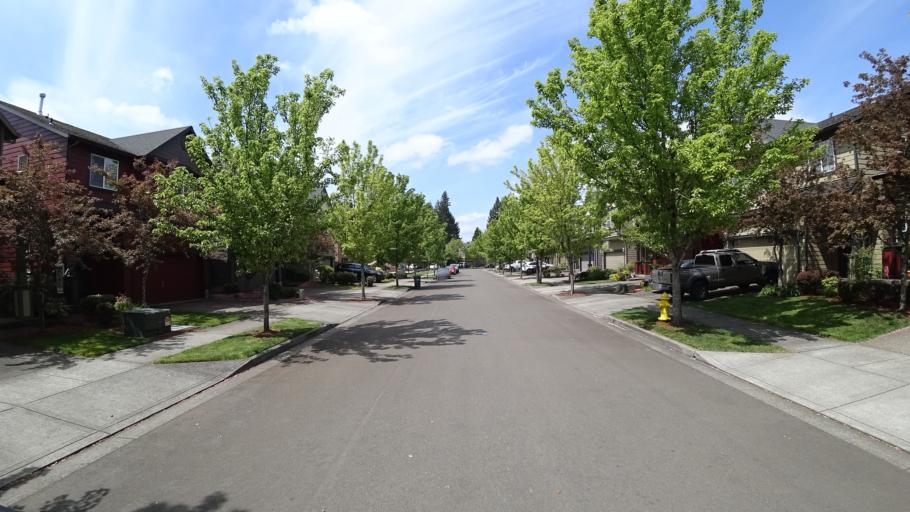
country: US
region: Oregon
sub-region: Washington County
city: Hillsboro
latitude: 45.5402
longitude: -122.9968
